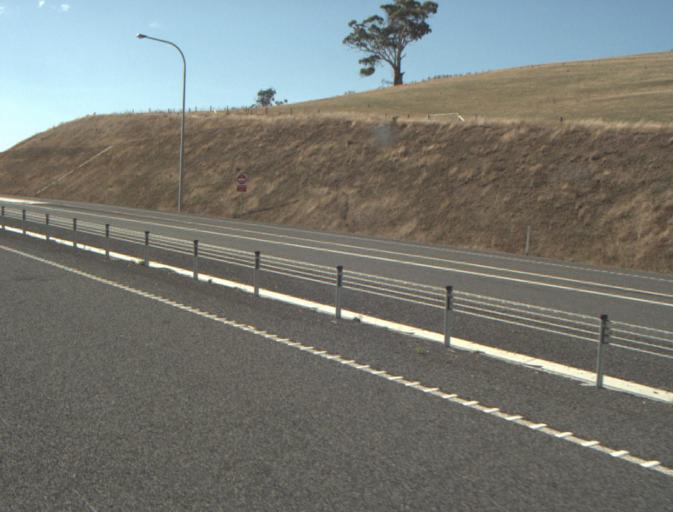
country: AU
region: Tasmania
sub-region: Launceston
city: Mayfield
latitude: -41.3568
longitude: 147.1053
